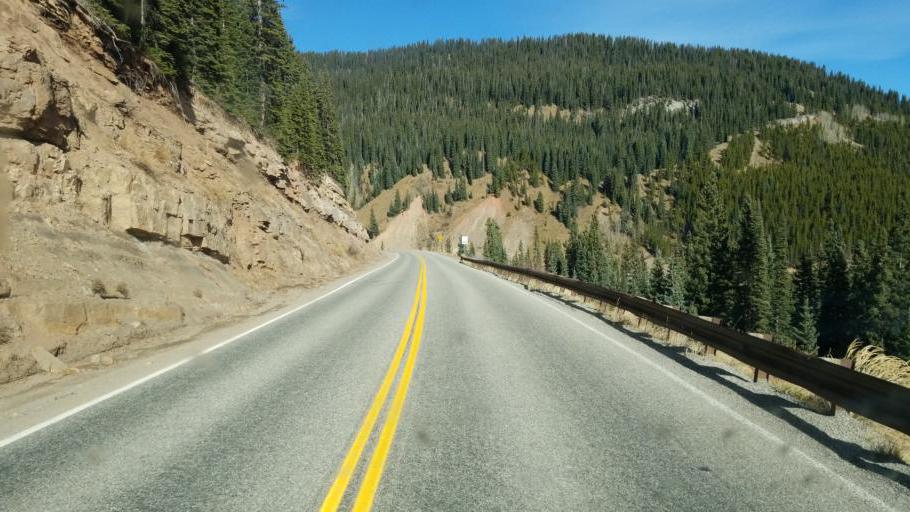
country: US
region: Colorado
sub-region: San Juan County
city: Silverton
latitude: 37.7038
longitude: -107.7683
